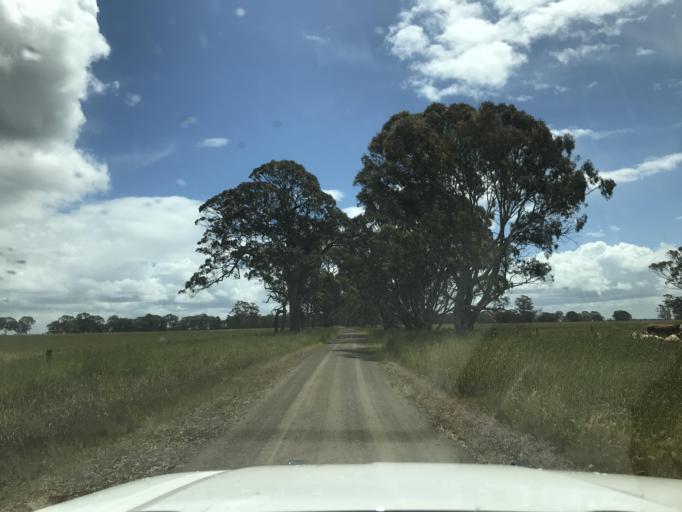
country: AU
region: South Australia
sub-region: Wattle Range
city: Penola
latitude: -37.1257
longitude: 141.3039
